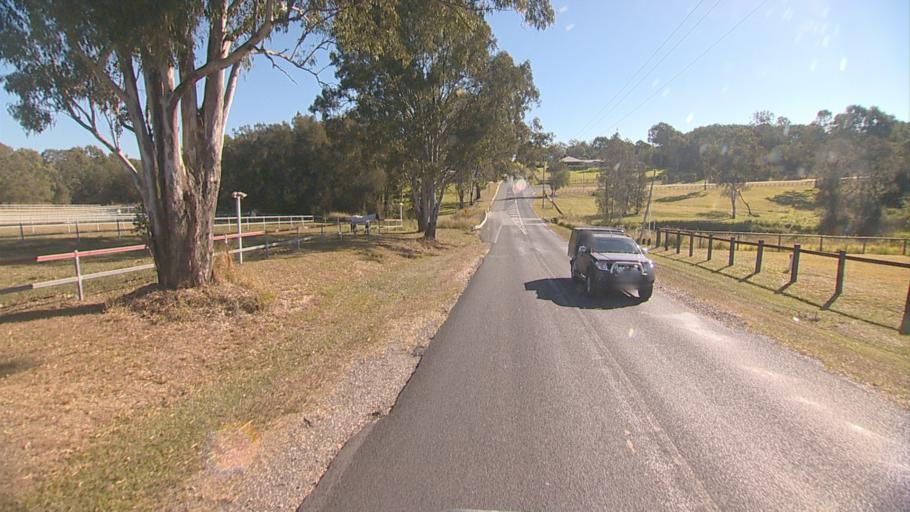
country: AU
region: Queensland
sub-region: Logan
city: Chambers Flat
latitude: -27.7777
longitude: 153.0942
